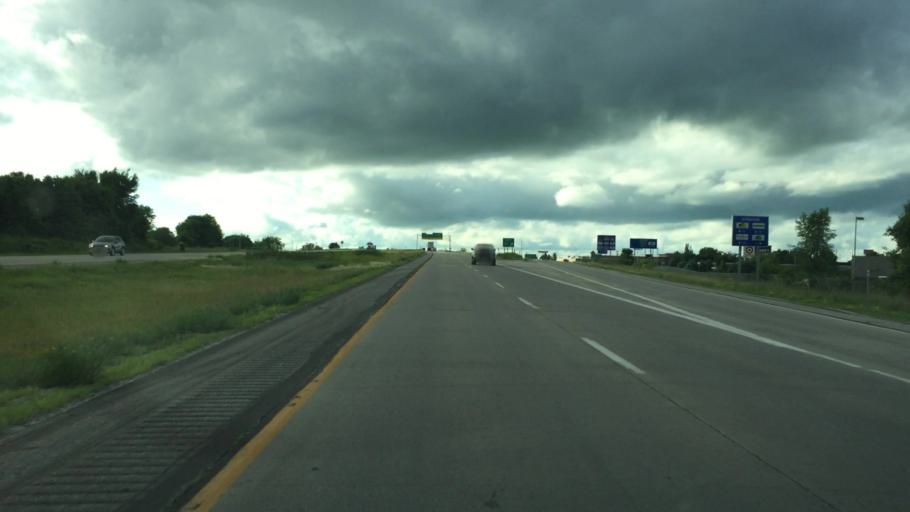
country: US
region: Iowa
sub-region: Polk County
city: Altoona
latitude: 41.6399
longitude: -93.5074
